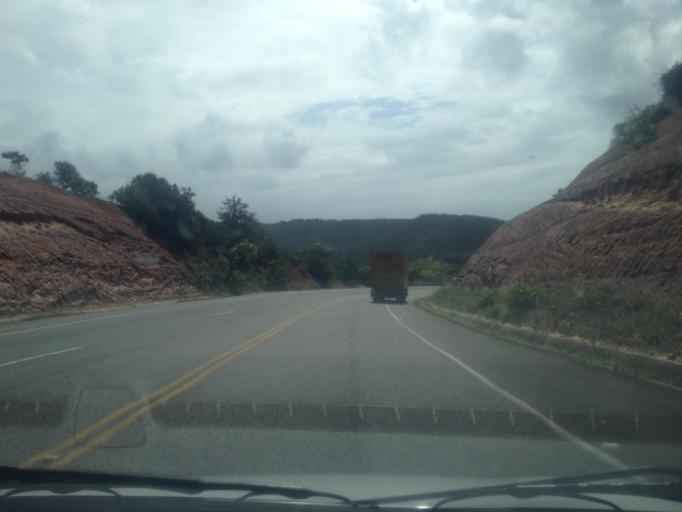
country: BR
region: Bahia
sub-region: Conde
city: Conde
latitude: -11.7339
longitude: -37.5805
